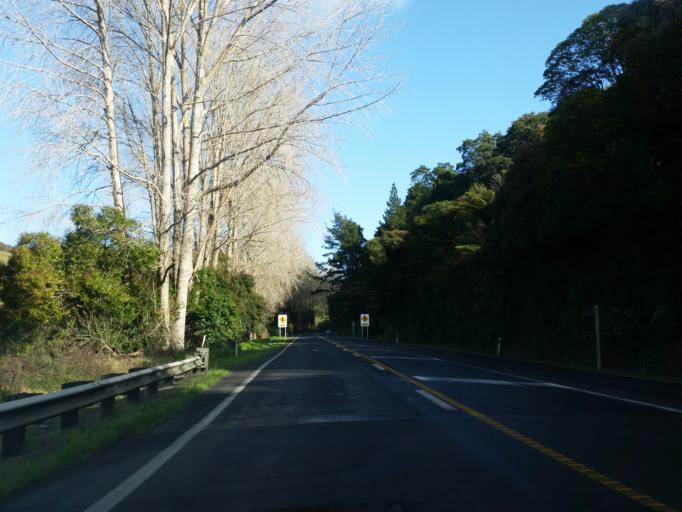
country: NZ
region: Waikato
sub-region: Hauraki District
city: Waihi
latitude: -37.4173
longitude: 175.7639
